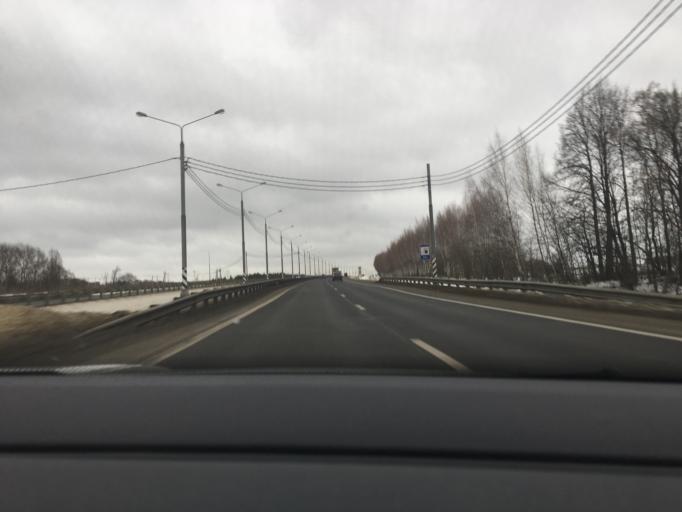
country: RU
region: Tula
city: Zaokskiy
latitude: 54.8118
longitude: 37.4813
